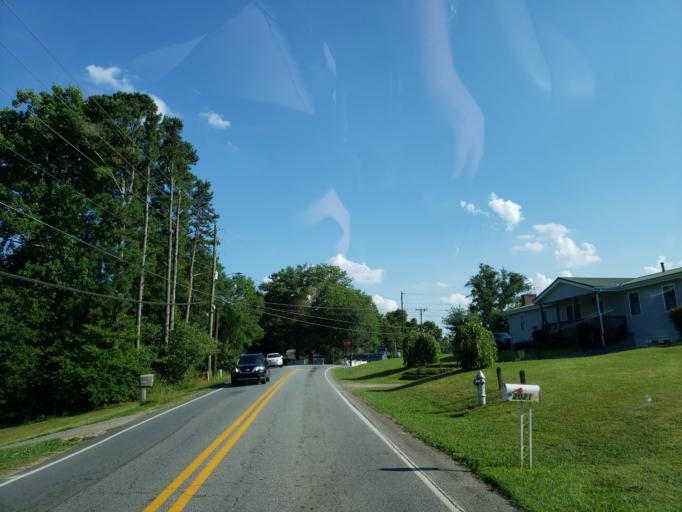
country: US
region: Georgia
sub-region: Cherokee County
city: Woodstock
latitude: 34.0903
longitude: -84.5475
